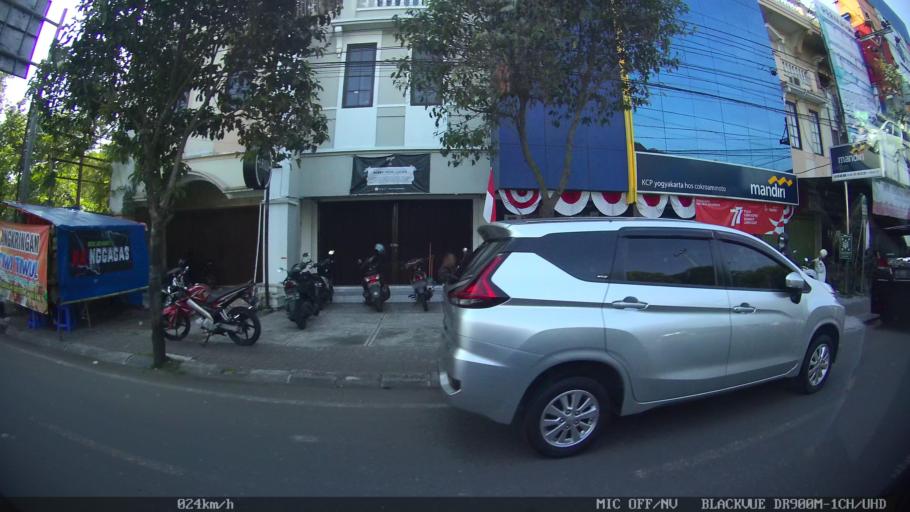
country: ID
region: Daerah Istimewa Yogyakarta
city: Yogyakarta
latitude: -7.7891
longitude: 110.3538
